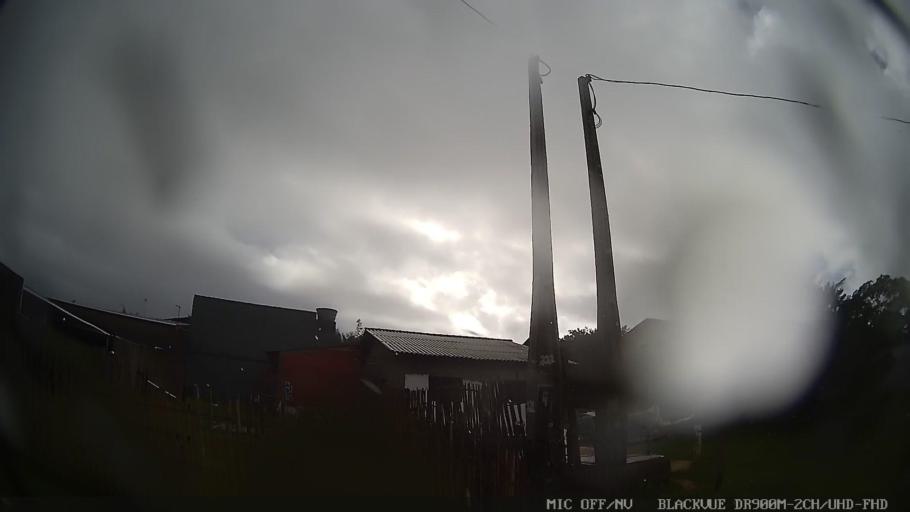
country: BR
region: Sao Paulo
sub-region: Peruibe
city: Peruibe
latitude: -24.2475
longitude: -46.8989
